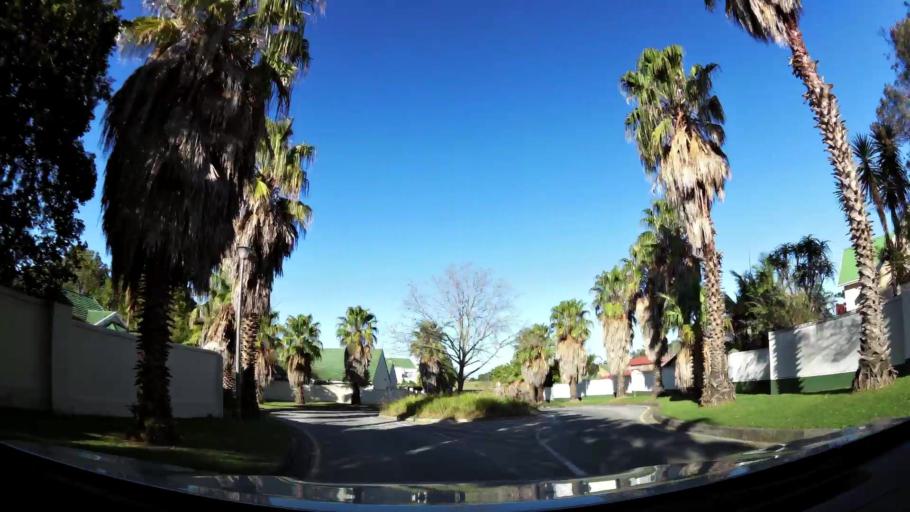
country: ZA
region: Western Cape
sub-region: Eden District Municipality
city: George
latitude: -33.9613
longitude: 22.4424
